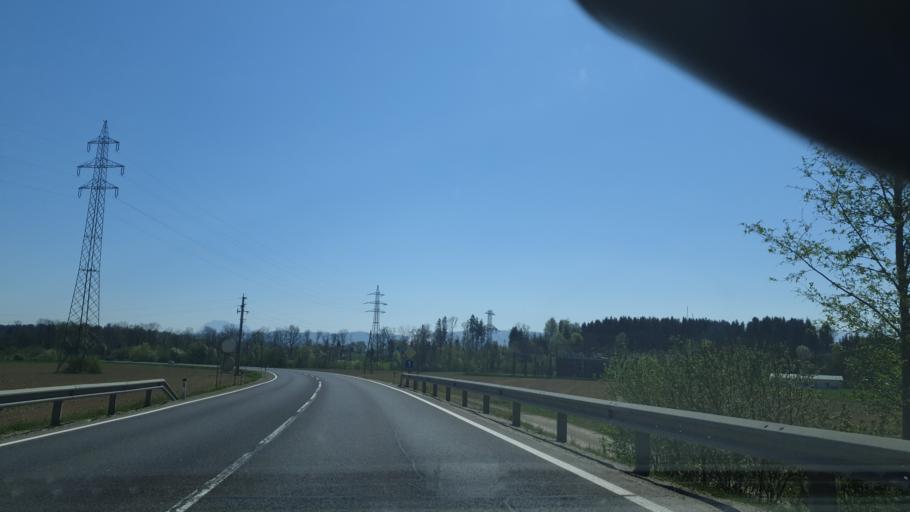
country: AT
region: Upper Austria
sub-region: Politischer Bezirk Vocklabruck
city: Timelkam
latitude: 47.9961
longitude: 13.5983
